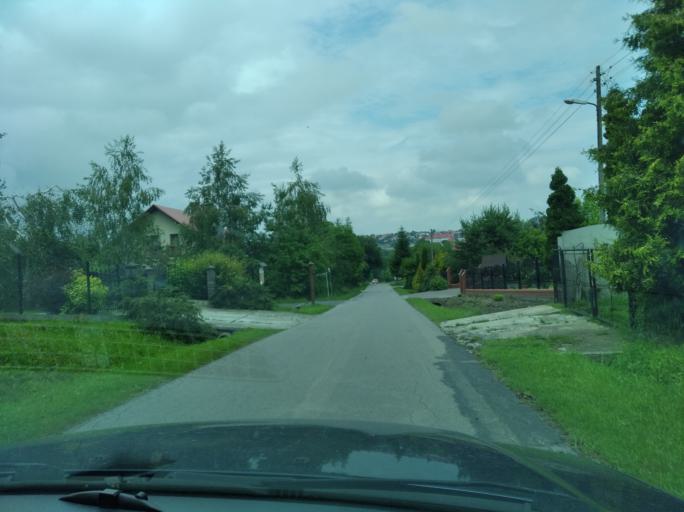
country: PL
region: Subcarpathian Voivodeship
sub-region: Powiat jaroslawski
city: Pruchnik
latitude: 49.8979
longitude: 22.5187
